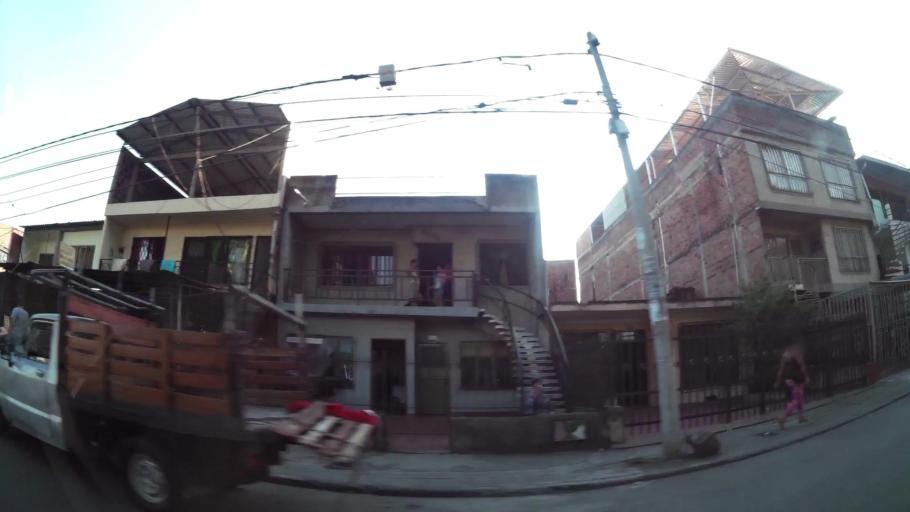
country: CO
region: Valle del Cauca
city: Cali
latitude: 3.4118
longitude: -76.5076
